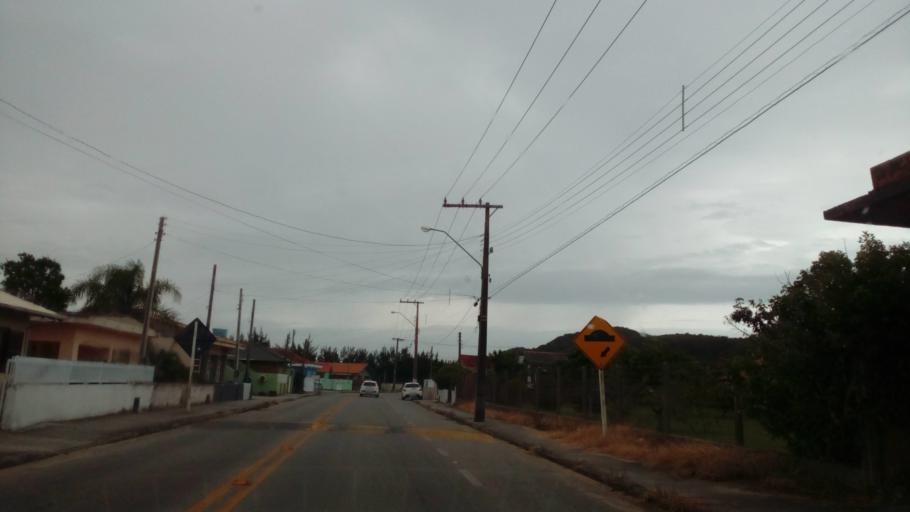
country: BR
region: Santa Catarina
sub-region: Laguna
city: Laguna
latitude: -28.5175
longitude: -48.7715
